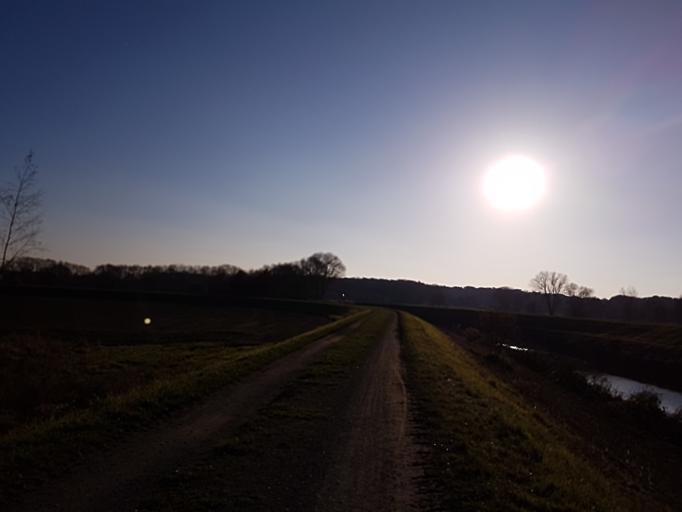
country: BE
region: Flanders
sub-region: Provincie Vlaams-Brabant
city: Boortmeerbeek
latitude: 50.9933
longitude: 4.6015
